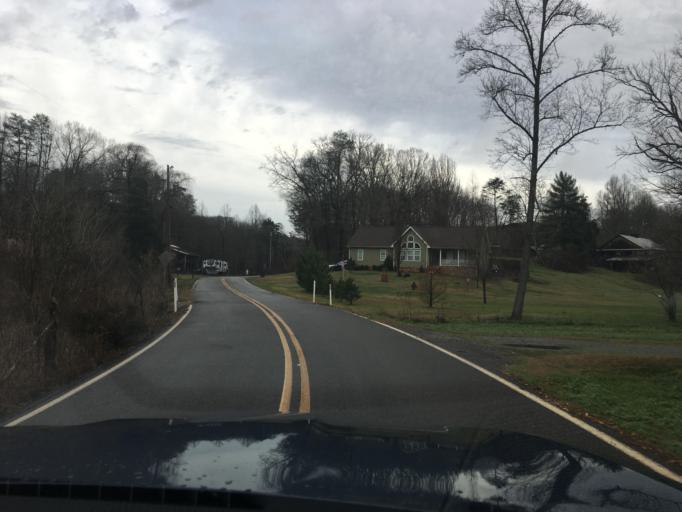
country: US
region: Tennessee
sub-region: McMinn County
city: Englewood
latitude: 35.3818
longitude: -84.4372
